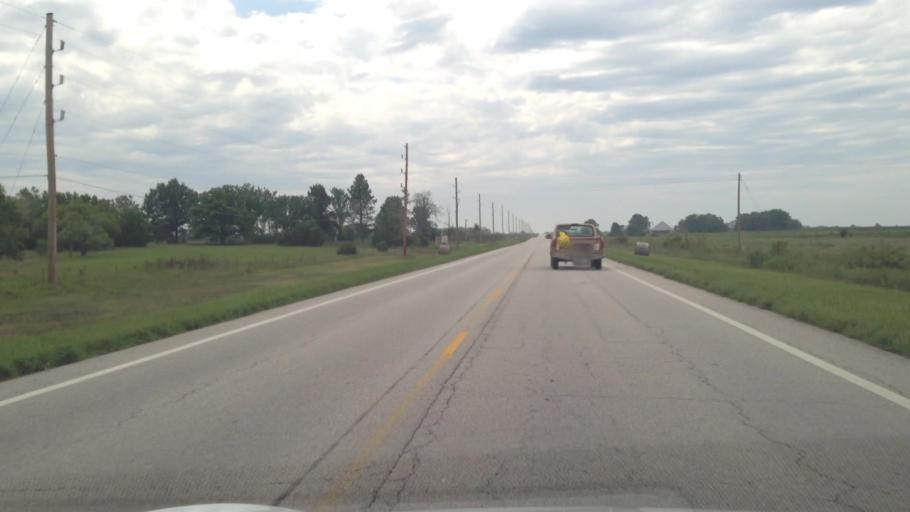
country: US
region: Kansas
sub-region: Allen County
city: Iola
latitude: 37.9474
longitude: -95.1700
